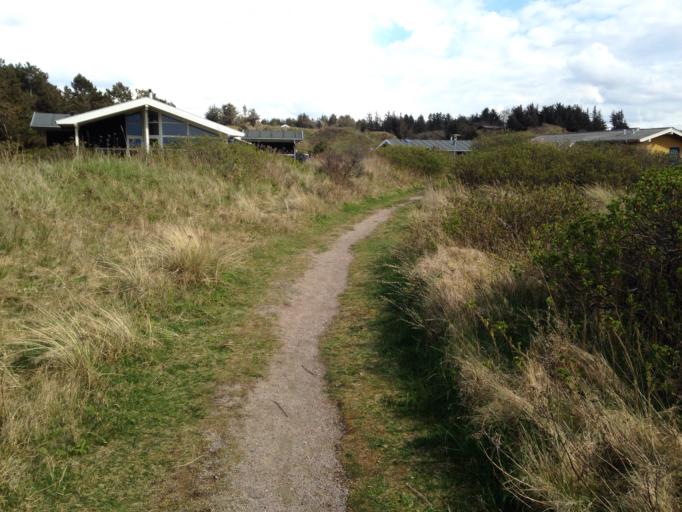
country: DK
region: North Denmark
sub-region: Hjorring Kommune
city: Hjorring
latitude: 57.4911
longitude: 9.8347
